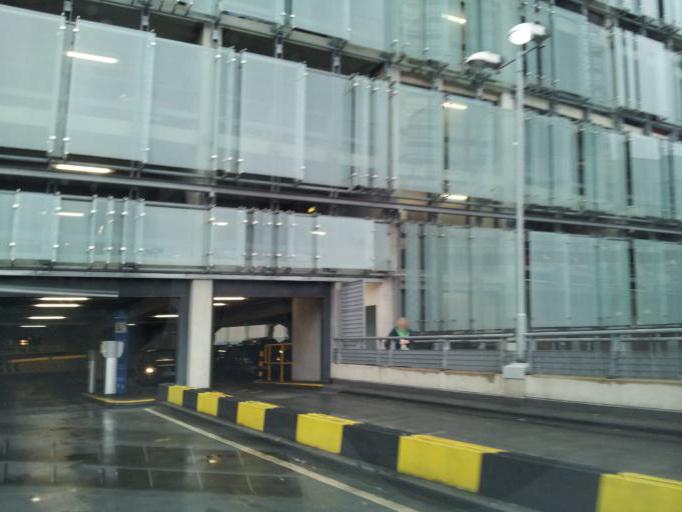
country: GB
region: England
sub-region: Manchester
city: Manchester
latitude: 53.4858
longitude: -2.2382
